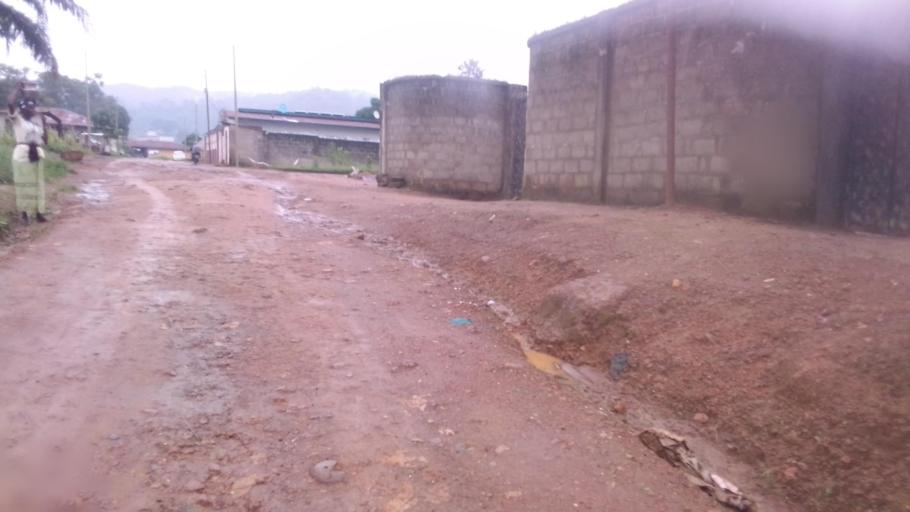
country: SL
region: Eastern Province
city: Kenema
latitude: 7.8866
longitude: -11.1788
